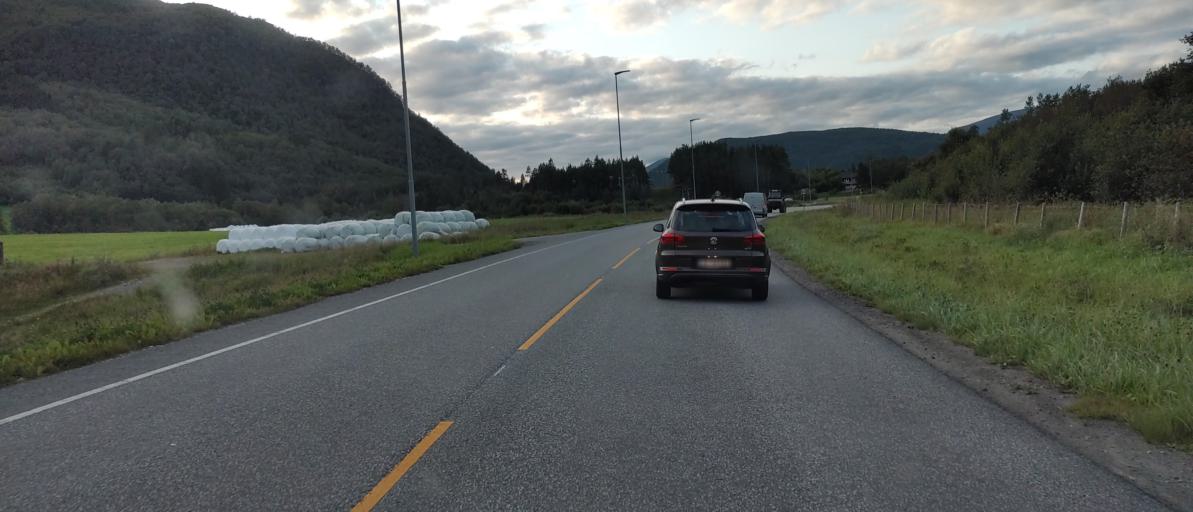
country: NO
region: More og Romsdal
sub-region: Molde
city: Molde
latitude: 62.7901
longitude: 7.2338
